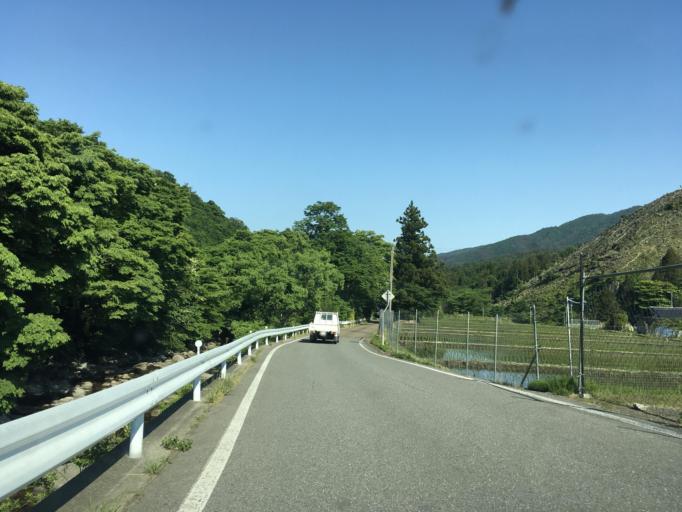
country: JP
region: Iwate
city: Kamaishi
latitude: 39.1959
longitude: 141.8369
